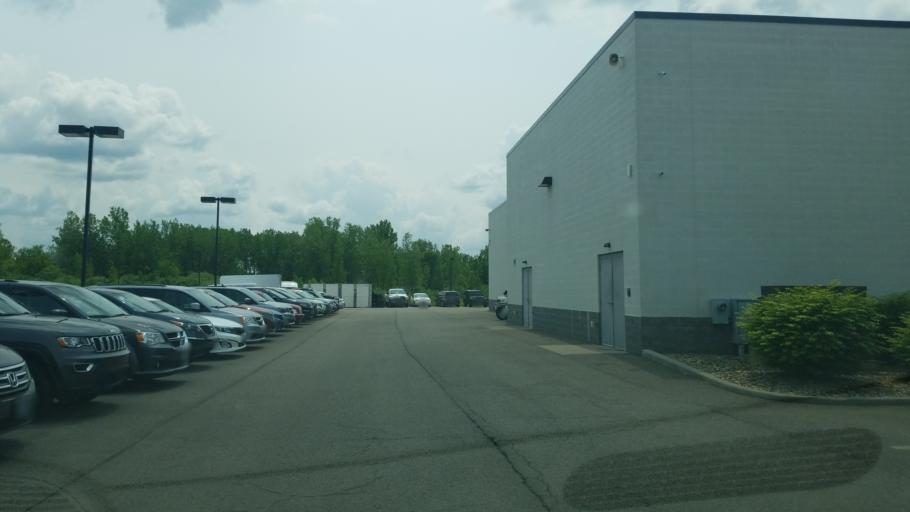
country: US
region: Ohio
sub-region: Richland County
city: Ontario
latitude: 40.7700
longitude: -82.5793
